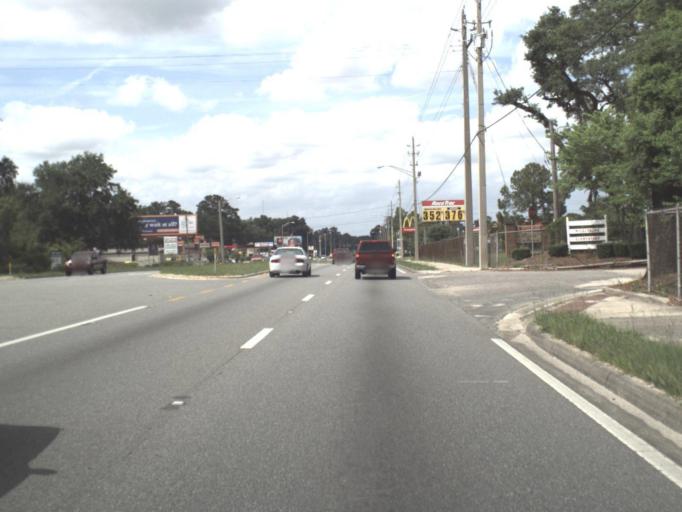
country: US
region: Florida
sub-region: Clay County
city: Middleburg
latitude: 30.0693
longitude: -81.8659
